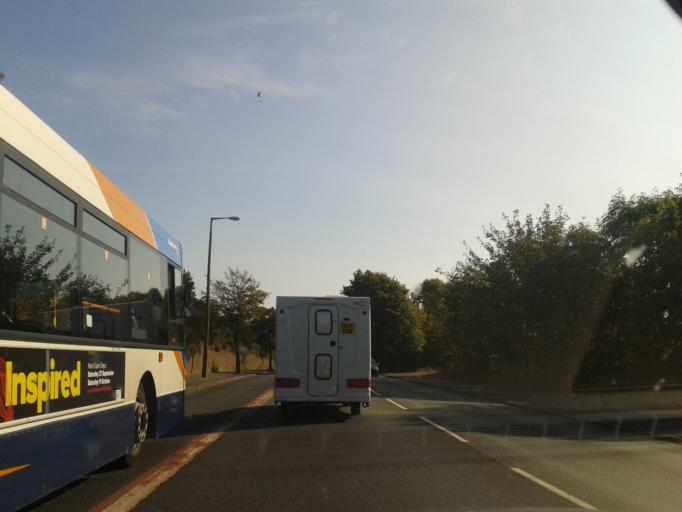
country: GB
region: England
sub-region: Lancashire
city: Lancaster
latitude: 54.0558
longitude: -2.8126
